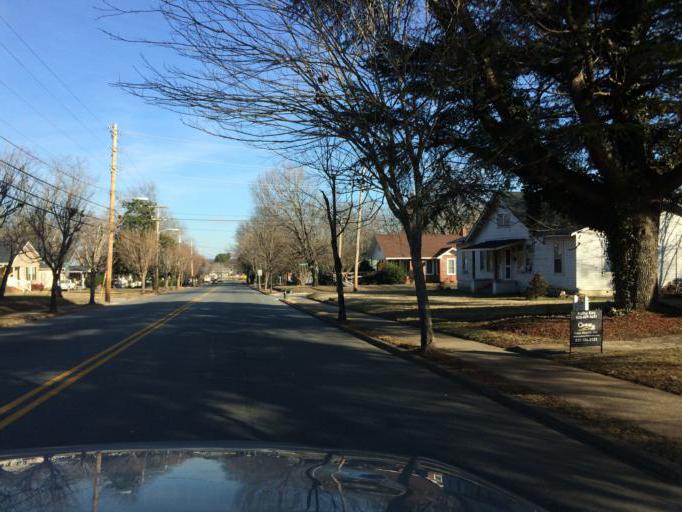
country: US
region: North Carolina
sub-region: Rutherford County
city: Forest City
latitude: 35.3322
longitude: -81.8550
